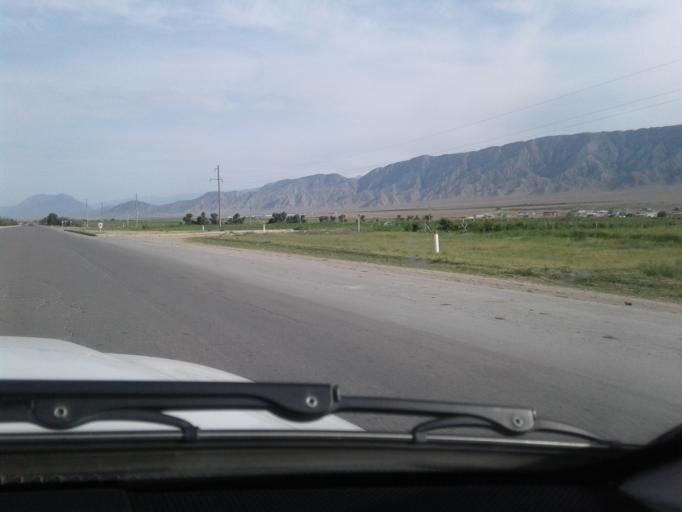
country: TM
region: Ahal
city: Arcabil
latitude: 38.2088
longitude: 57.8157
